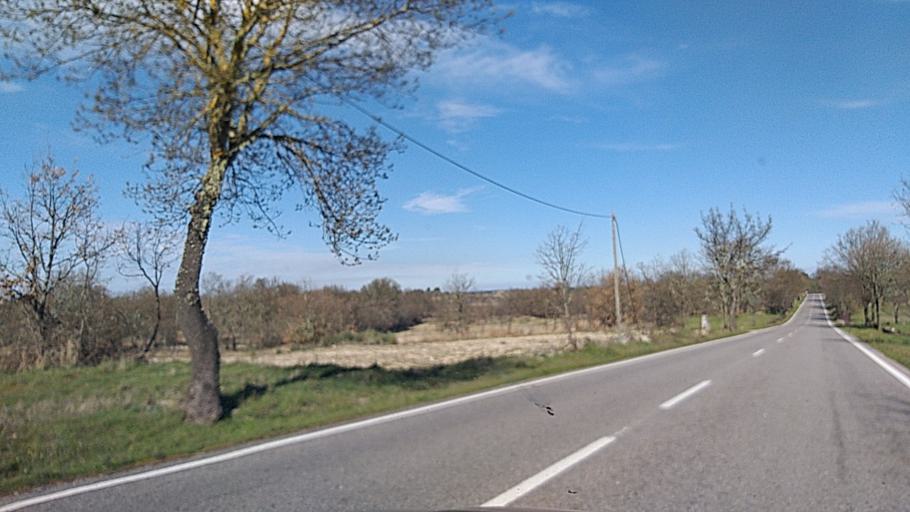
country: PT
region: Guarda
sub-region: Guarda
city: Sequeira
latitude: 40.5966
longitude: -7.1213
